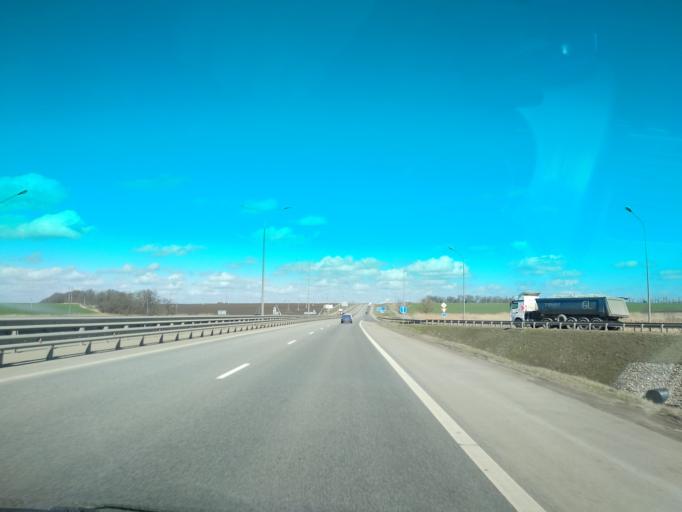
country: RU
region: Krasnodarskiy
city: Korenovsk
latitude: 45.4851
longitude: 39.4102
